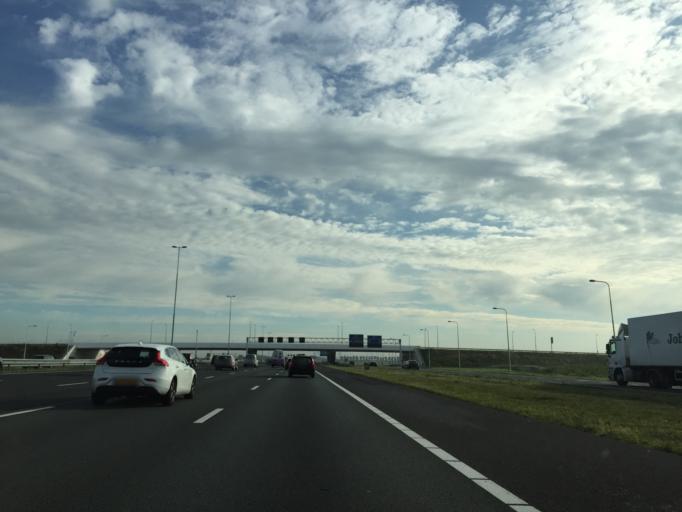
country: NL
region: North Holland
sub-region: Gemeente Haarlemmermeer
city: Hoofddorp
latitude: 52.2703
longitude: 4.7014
